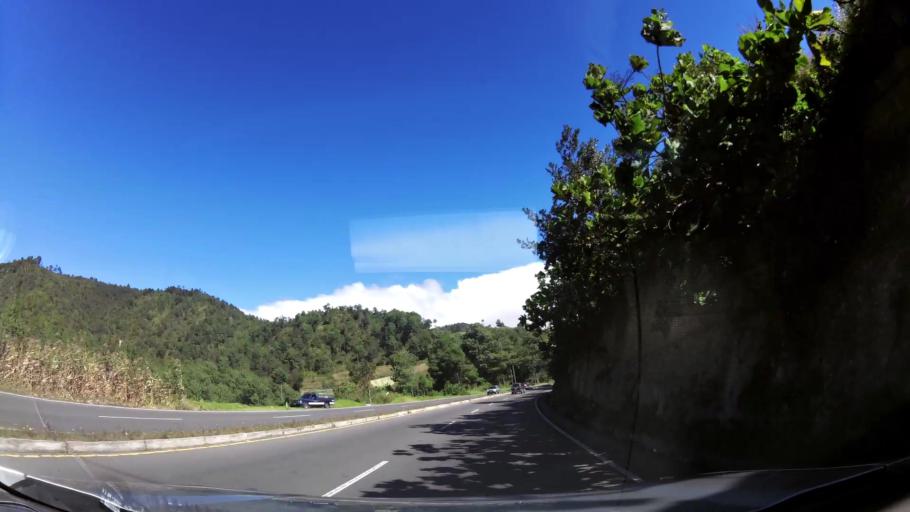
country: GT
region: Solola
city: Solola
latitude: 14.8190
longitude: -91.2018
